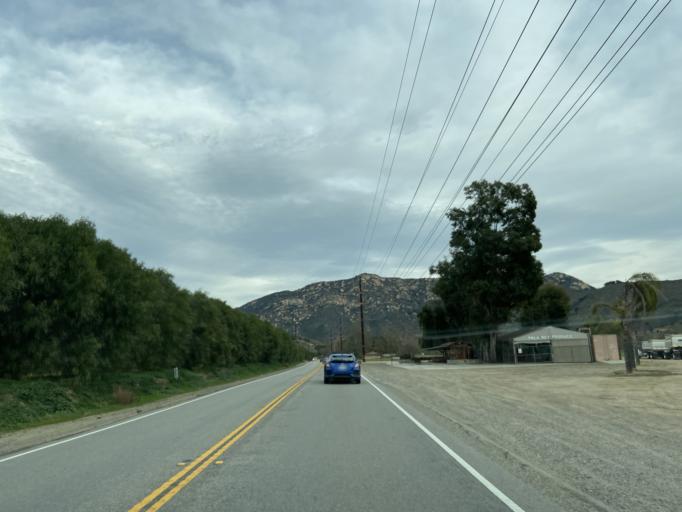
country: US
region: California
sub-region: San Diego County
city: Rainbow
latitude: 33.3437
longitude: -117.1301
